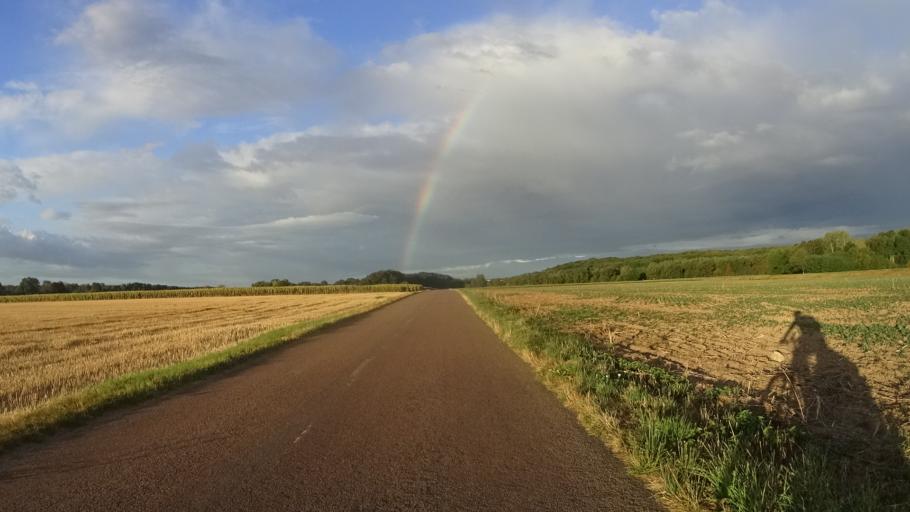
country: FR
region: Bourgogne
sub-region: Departement de la Cote-d'Or
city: Seurre
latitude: 46.9639
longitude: 5.0805
